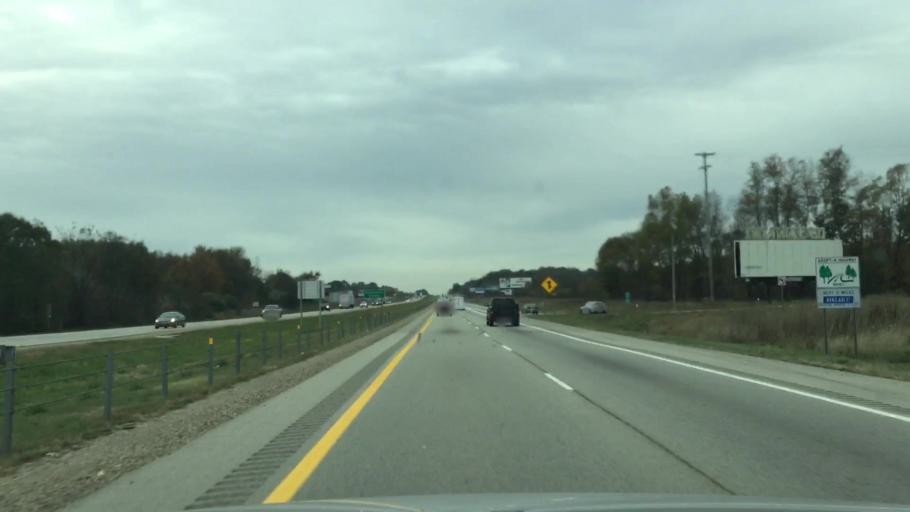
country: US
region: Michigan
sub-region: Calhoun County
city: Springfield
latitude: 42.2728
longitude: -85.2962
